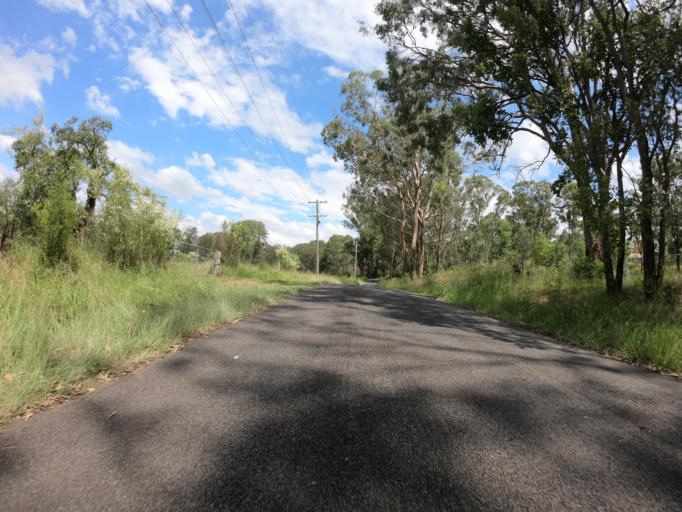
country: AU
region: New South Wales
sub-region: Penrith Municipality
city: Mulgoa
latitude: -33.8286
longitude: 150.6567
